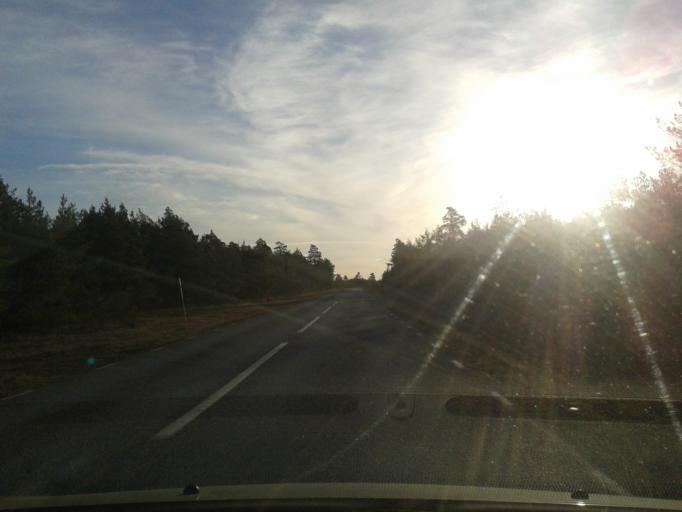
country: SE
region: Gotland
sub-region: Gotland
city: Hemse
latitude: 57.4040
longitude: 18.6373
